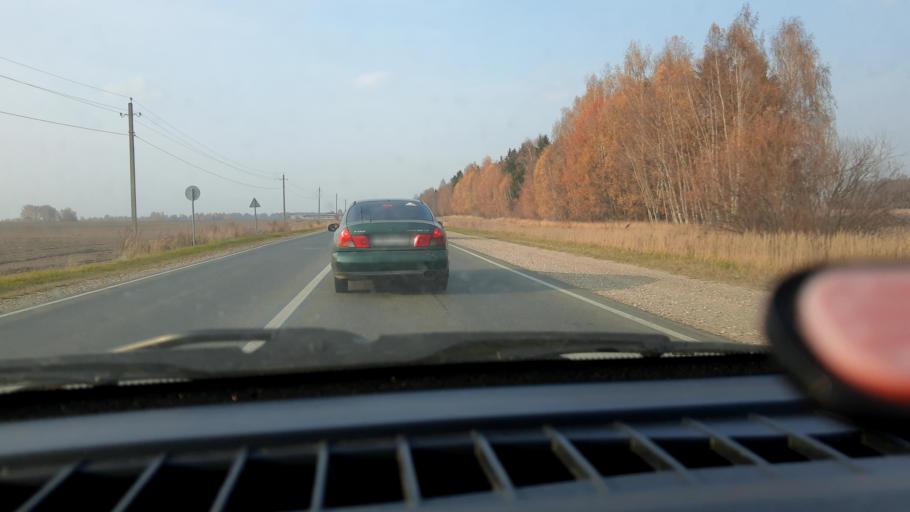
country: RU
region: Nizjnij Novgorod
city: Gorodets
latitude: 56.6176
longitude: 43.5586
